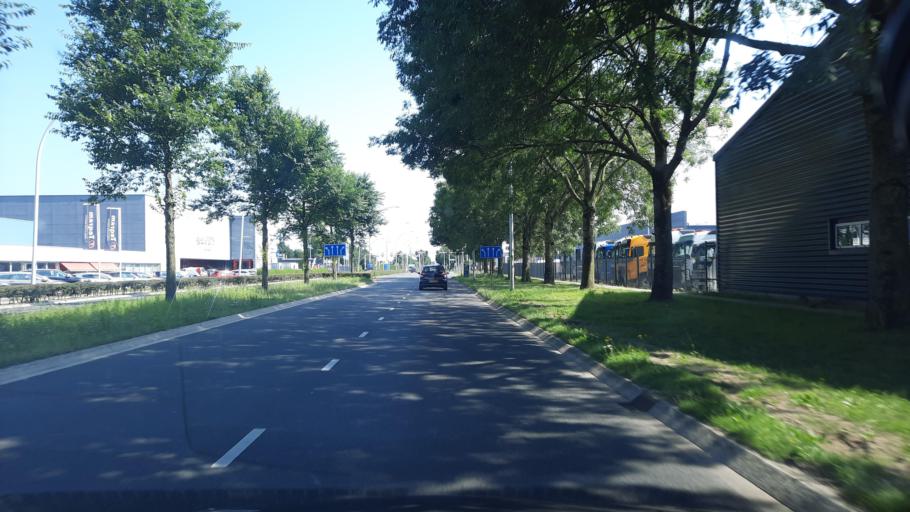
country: NL
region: Gelderland
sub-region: Gemeente Hattem
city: Hattem
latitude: 52.5146
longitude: 6.0518
